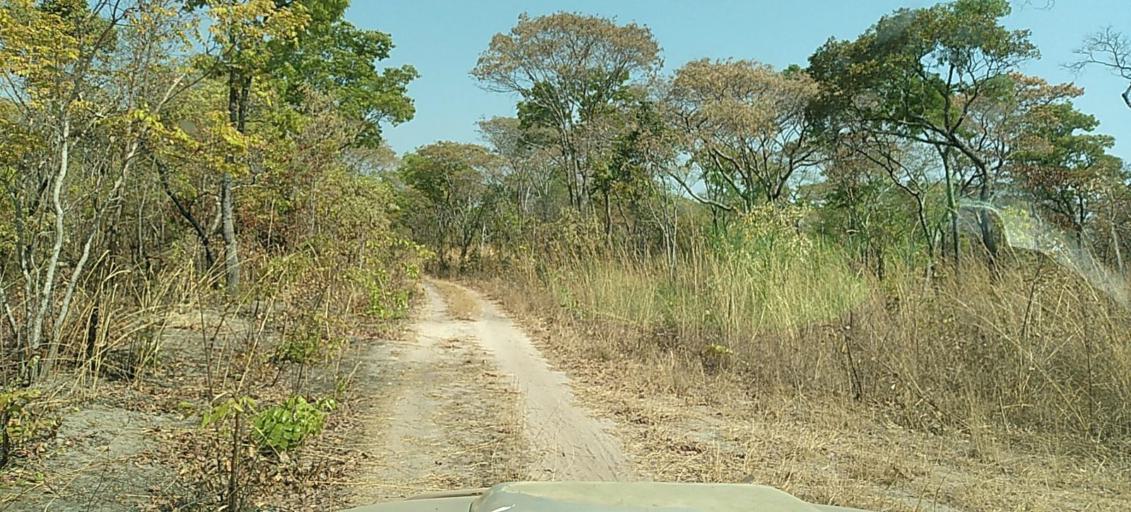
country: ZM
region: North-Western
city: Kalengwa
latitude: -13.3319
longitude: 24.8444
